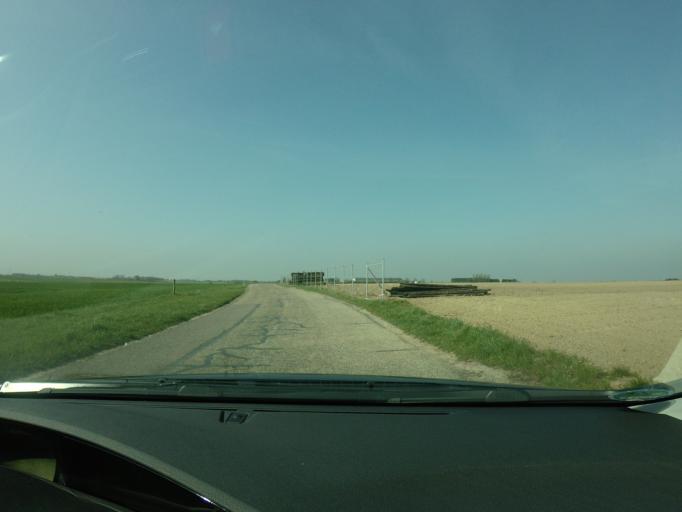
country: NL
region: Limburg
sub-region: Valkenburg aan de Geul
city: Houthem
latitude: 50.9036
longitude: 5.8063
